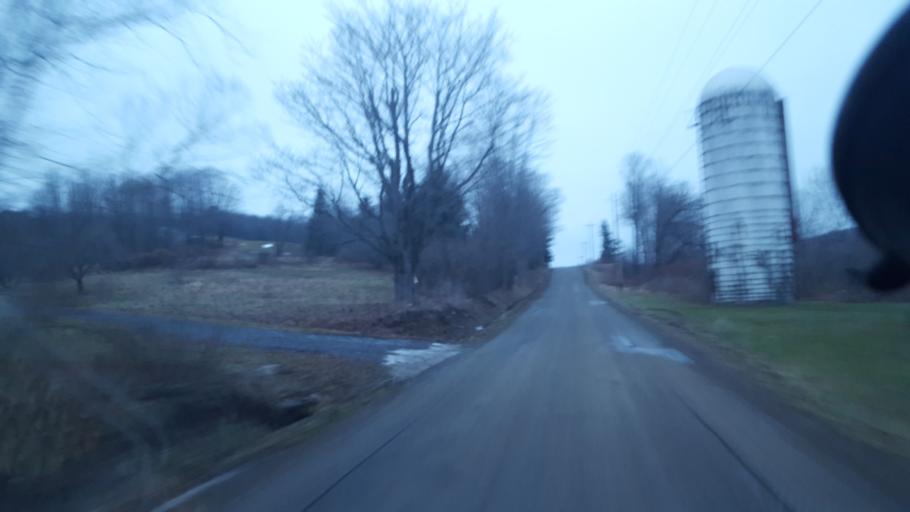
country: US
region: Pennsylvania
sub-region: Tioga County
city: Westfield
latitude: 41.9679
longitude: -77.7181
